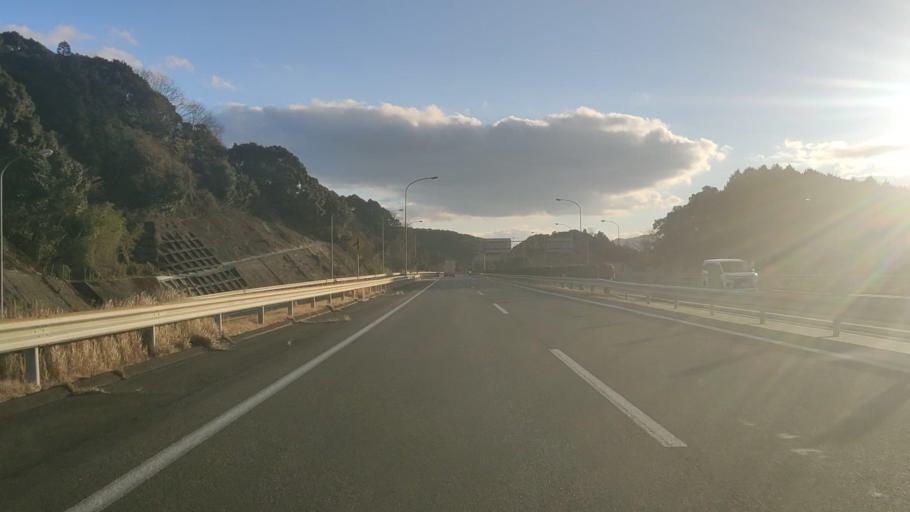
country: JP
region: Saga Prefecture
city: Ureshinomachi-shimojuku
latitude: 33.1460
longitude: 129.9978
